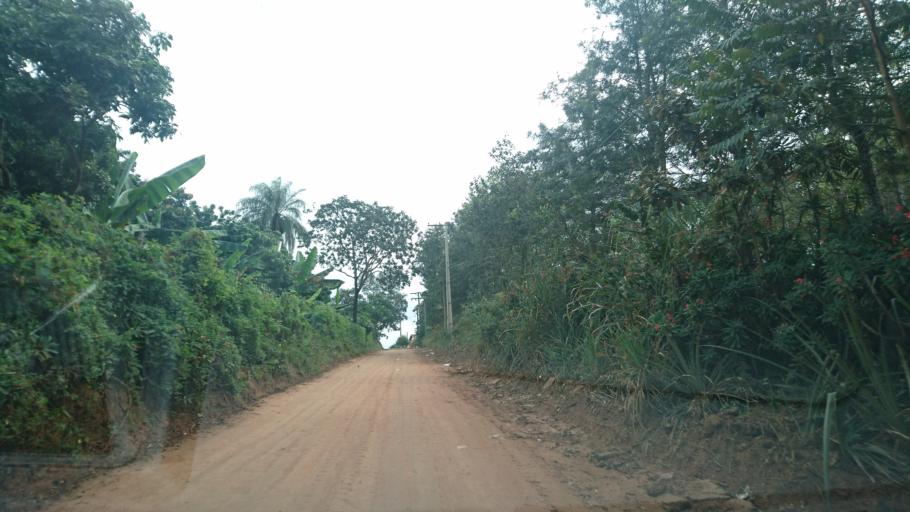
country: BR
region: Sao Paulo
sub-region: Casa Branca
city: Casa Branca
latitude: -21.7884
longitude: -47.0898
